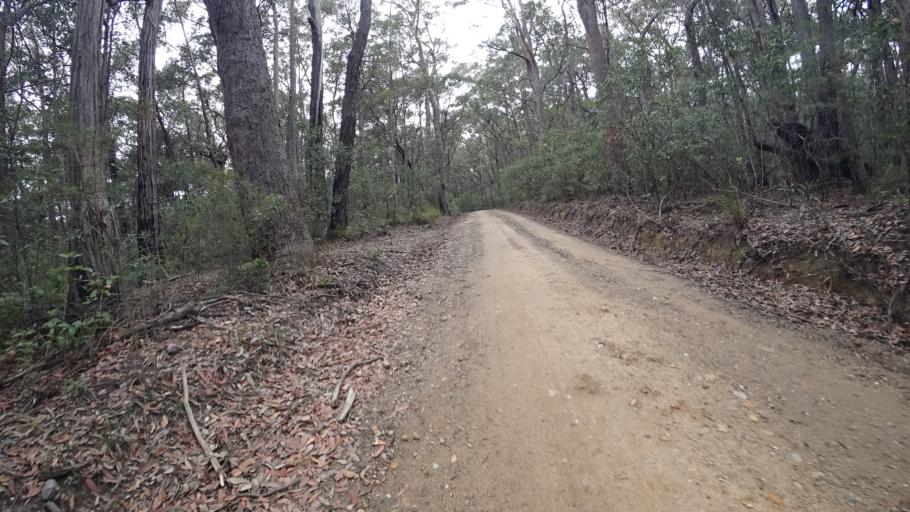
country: AU
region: New South Wales
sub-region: Shoalhaven Shire
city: Milton
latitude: -35.1703
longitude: 150.3801
